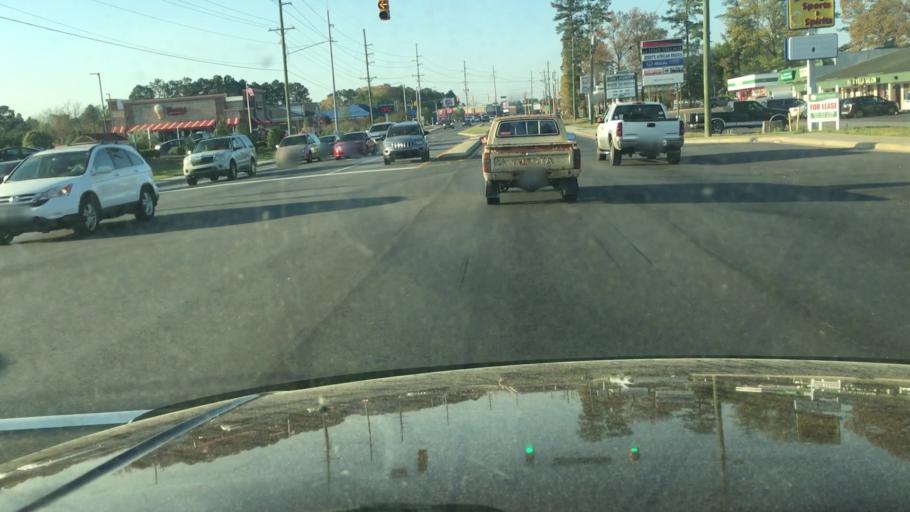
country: US
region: North Carolina
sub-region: Cumberland County
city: Fayetteville
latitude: 35.1261
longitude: -78.8792
